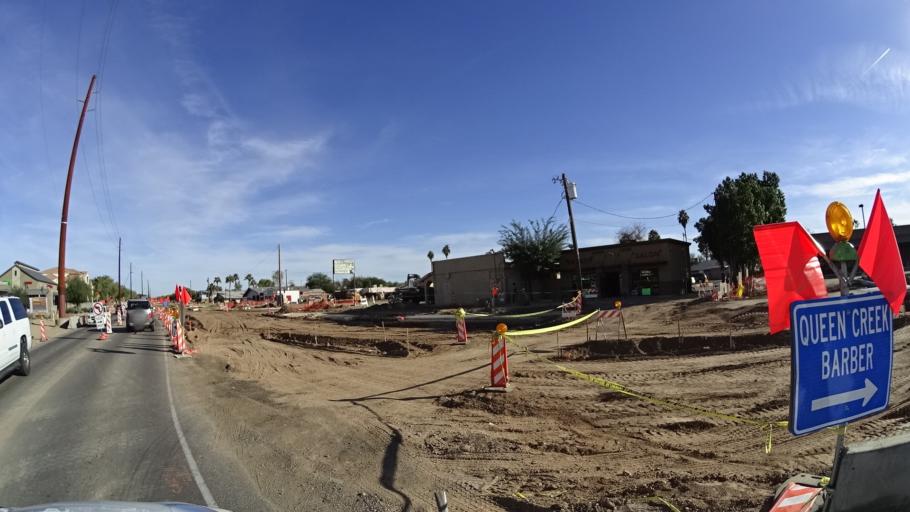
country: US
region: Arizona
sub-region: Maricopa County
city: Queen Creek
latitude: 33.2488
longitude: -111.6335
